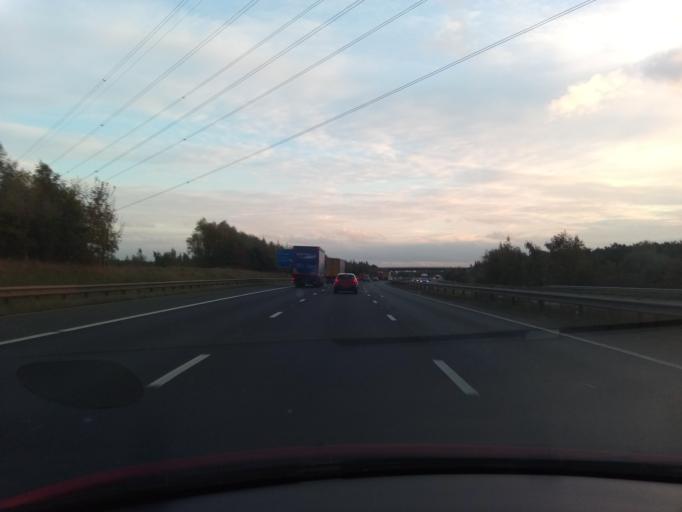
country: GB
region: England
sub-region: City and Borough of Leeds
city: Wetherby
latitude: 53.9559
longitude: -1.3692
